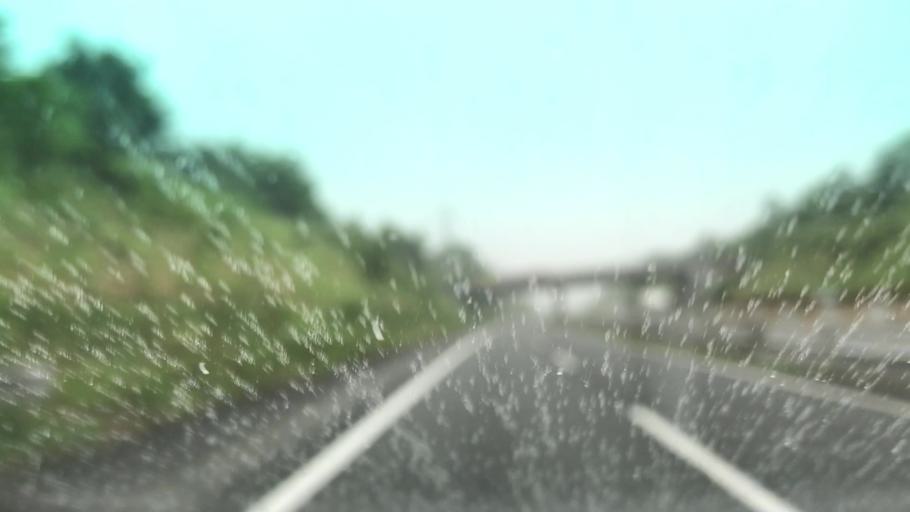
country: JP
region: Hokkaido
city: Tomakomai
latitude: 42.6195
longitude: 141.4760
